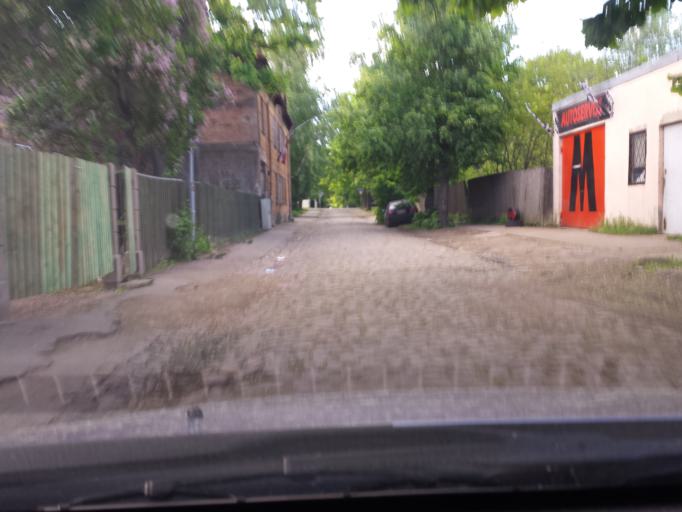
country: LV
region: Riga
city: Jaunciems
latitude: 56.9820
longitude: 24.1739
